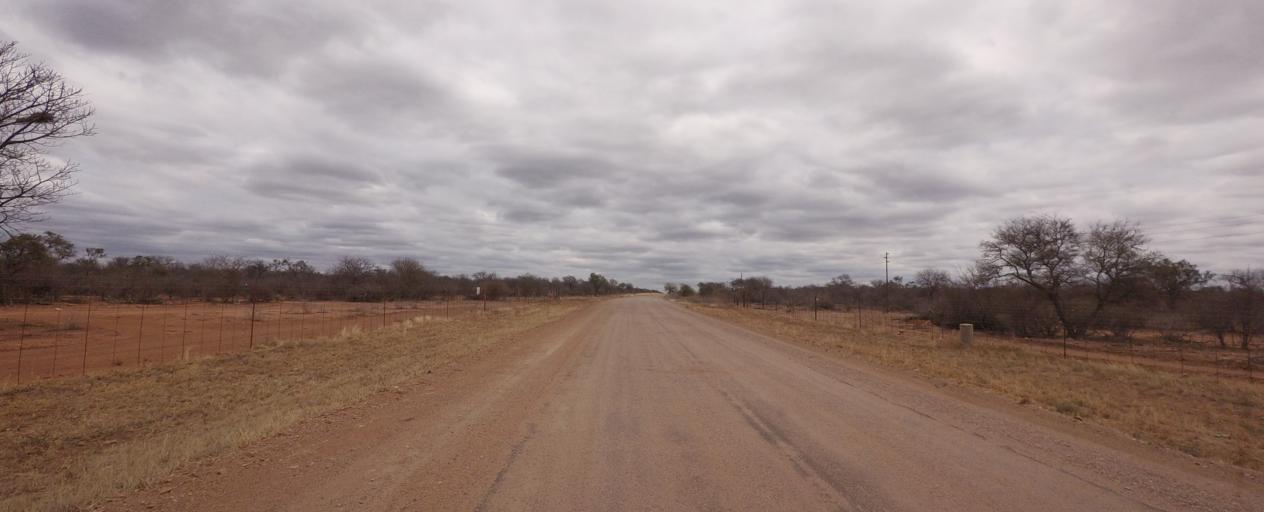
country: BW
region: Central
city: Mathathane
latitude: -22.7030
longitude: 28.6106
